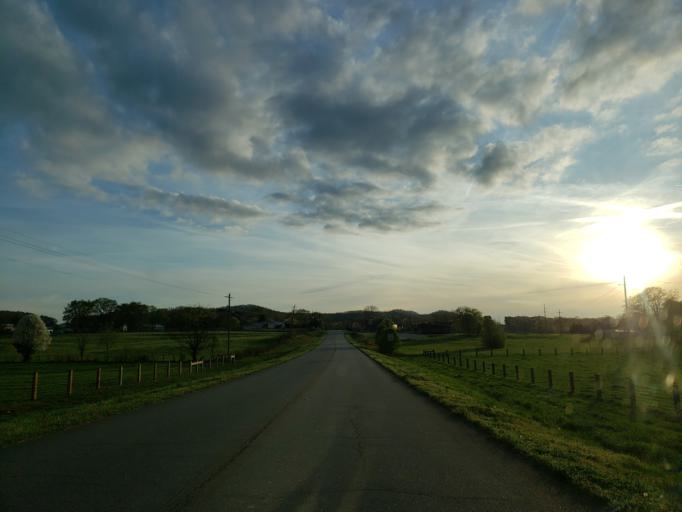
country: US
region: Georgia
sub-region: Bartow County
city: Euharlee
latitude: 34.0863
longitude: -84.9767
